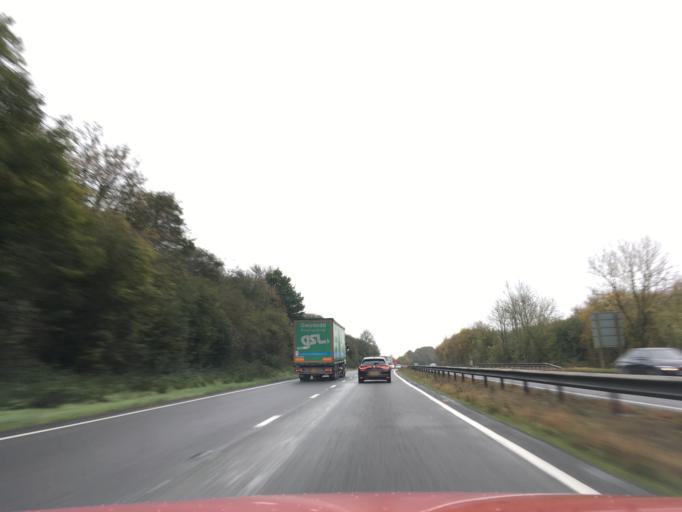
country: GB
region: England
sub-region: Hampshire
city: Highclere
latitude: 51.2919
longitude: -1.3377
